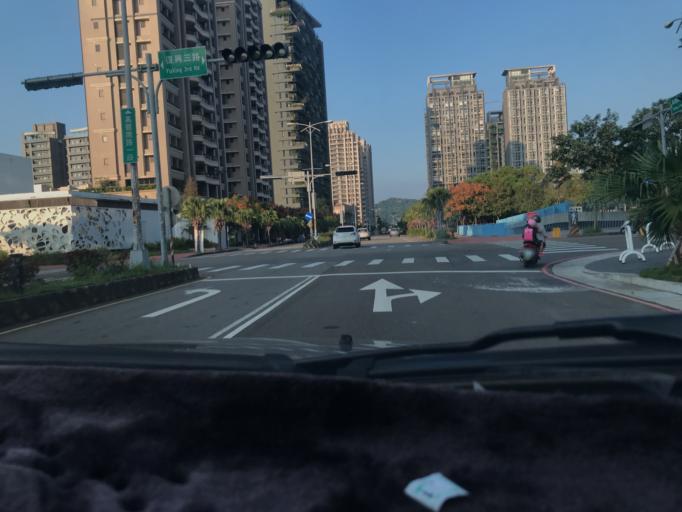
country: TW
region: Taiwan
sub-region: Hsinchu
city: Zhubei
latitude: 24.8095
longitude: 121.0335
